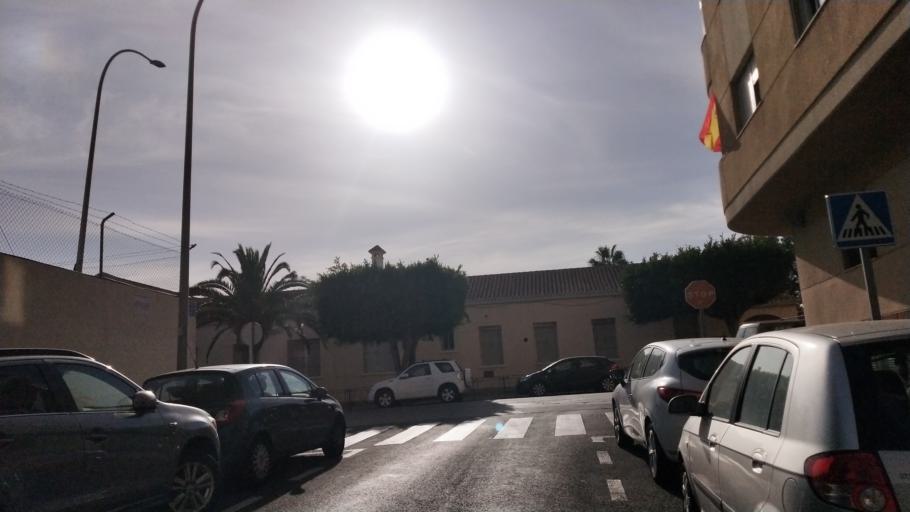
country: ES
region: Melilla
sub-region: Melilla
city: Melilla
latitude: 35.2874
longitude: -2.9483
